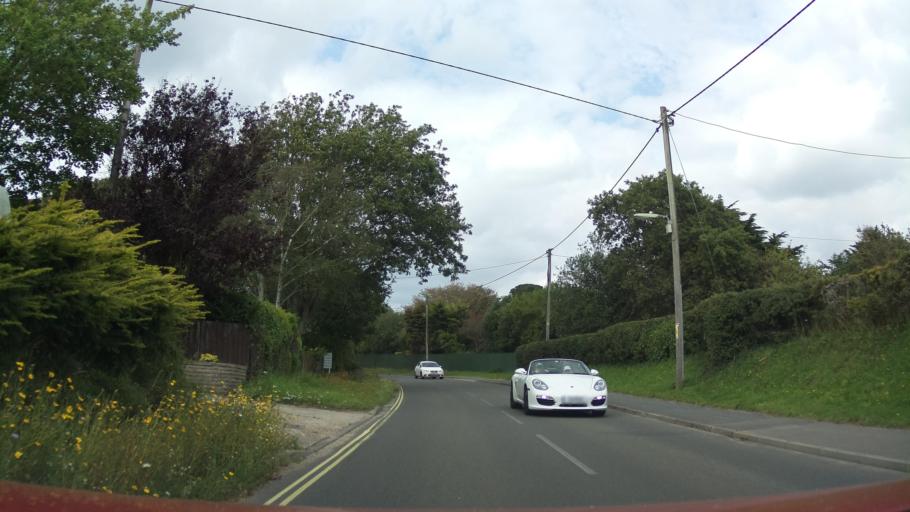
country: GB
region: England
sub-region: Hampshire
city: Milford on Sea
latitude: 50.7301
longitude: -1.5887
